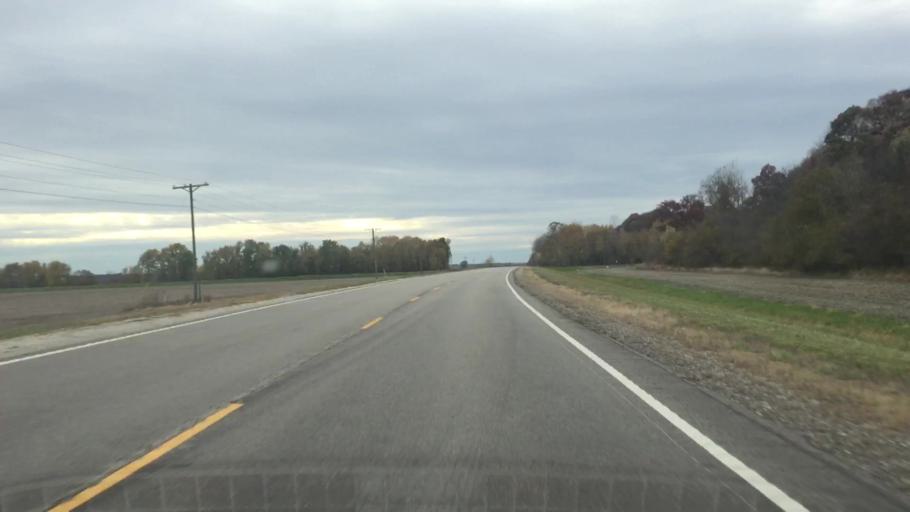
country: US
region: Missouri
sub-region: Callaway County
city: Holts Summit
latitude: 38.5829
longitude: -92.0580
